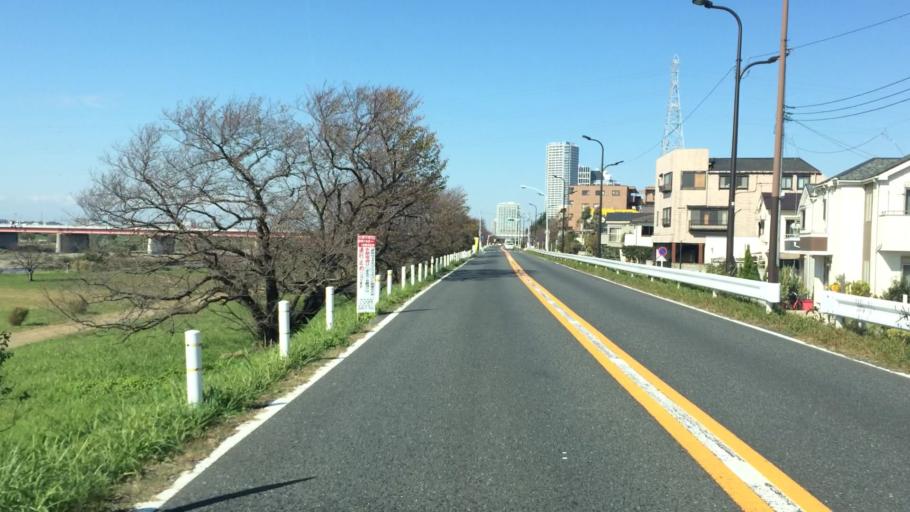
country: JP
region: Tokyo
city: Tokyo
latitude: 35.6012
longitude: 139.6412
